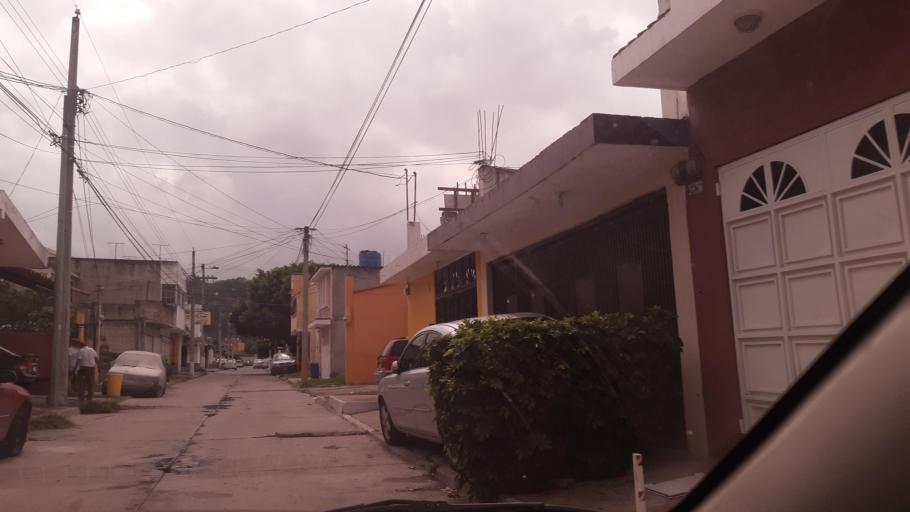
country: GT
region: Guatemala
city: Petapa
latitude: 14.5036
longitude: -90.5454
